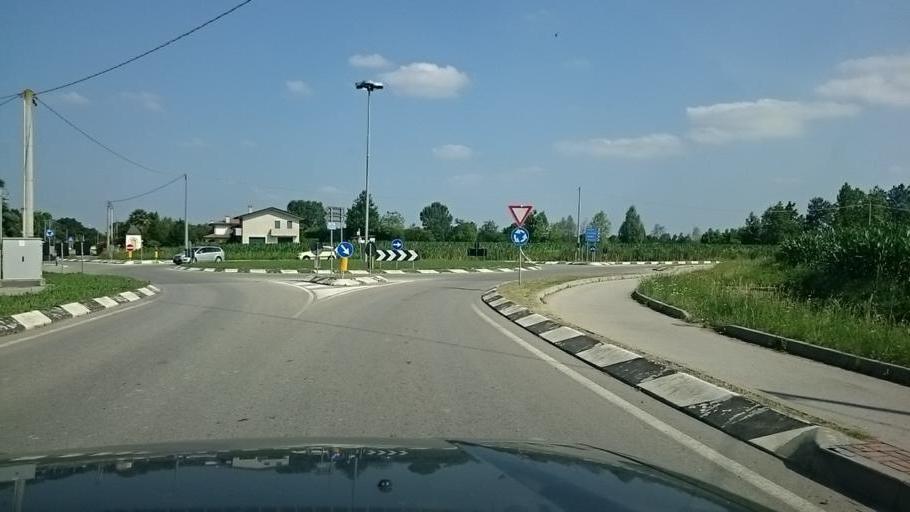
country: IT
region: Veneto
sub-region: Provincia di Padova
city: Villa del Conte
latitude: 45.5882
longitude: 11.8689
